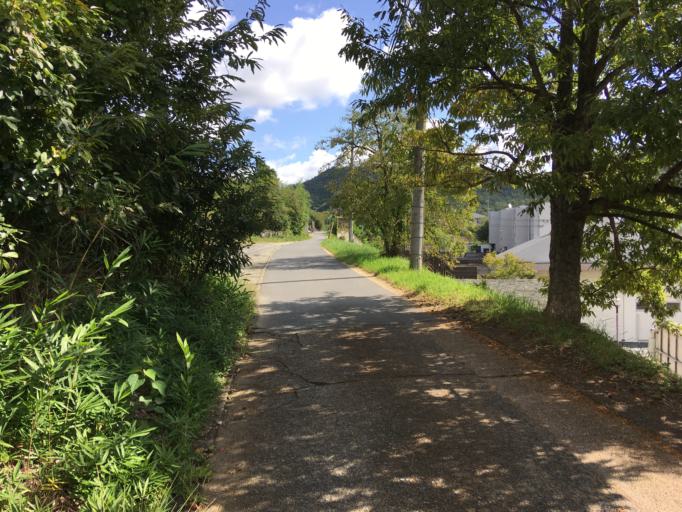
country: JP
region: Nara
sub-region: Ikoma-shi
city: Ikoma
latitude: 34.6417
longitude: 135.7044
